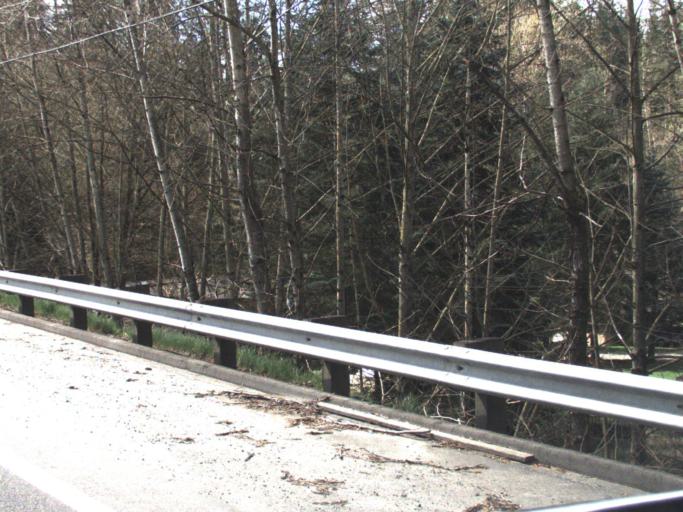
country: US
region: Washington
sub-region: King County
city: Maple Valley
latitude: 47.4050
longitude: -122.0403
